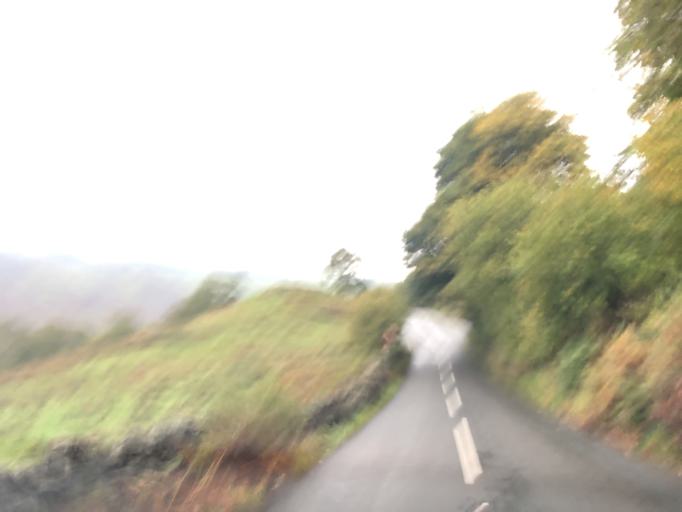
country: GB
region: England
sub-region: Cumbria
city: Windermere
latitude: 54.4353
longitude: -2.9020
